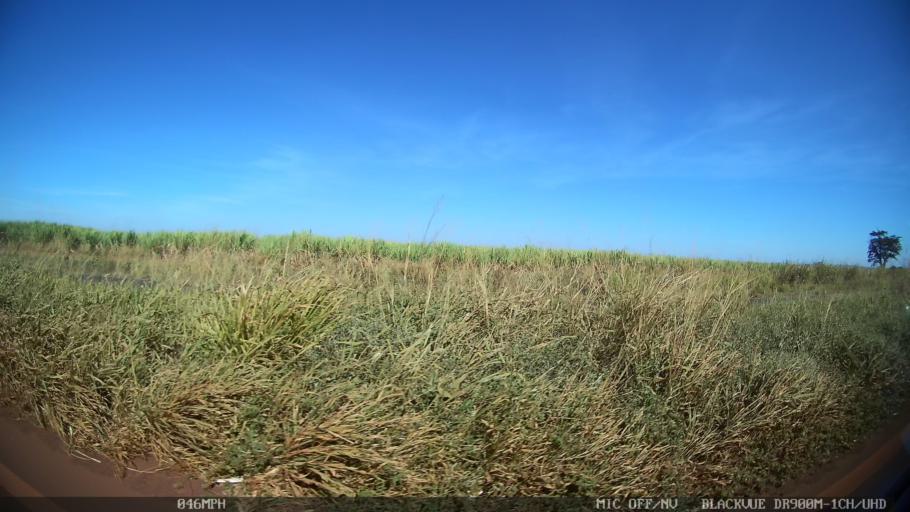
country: BR
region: Sao Paulo
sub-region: Barretos
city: Barretos
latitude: -20.4467
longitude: -48.4465
